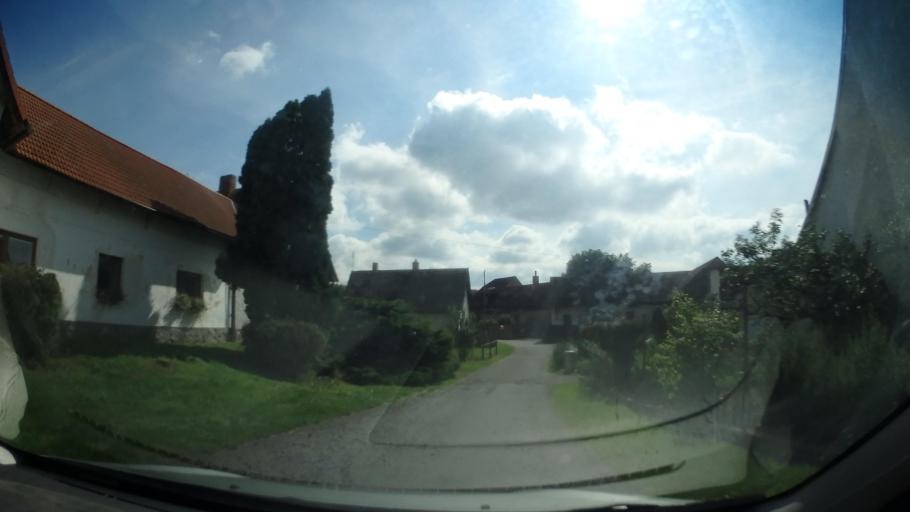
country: CZ
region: Central Bohemia
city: Krasna Hora nad Vltavou
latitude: 49.6760
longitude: 14.3209
